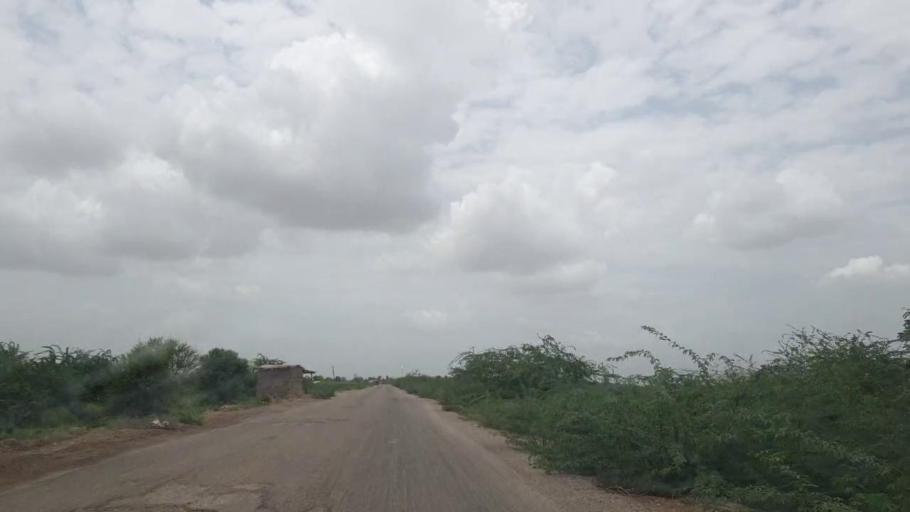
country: PK
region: Sindh
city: Naukot
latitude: 24.9214
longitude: 69.2733
